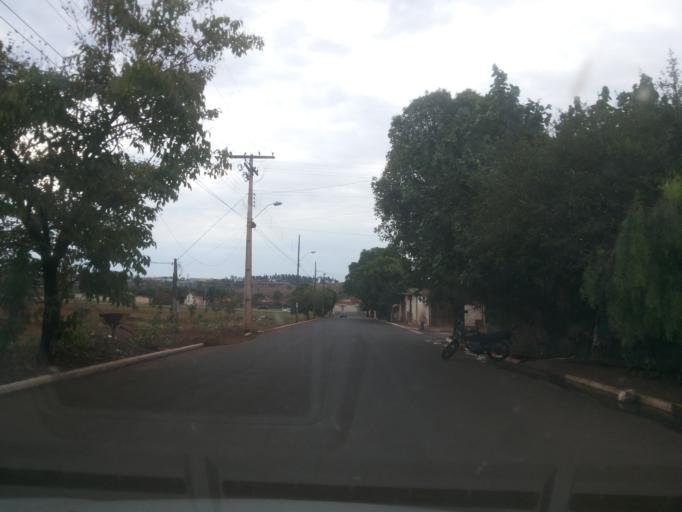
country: BR
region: Minas Gerais
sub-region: Ituiutaba
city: Ituiutaba
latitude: -18.9728
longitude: -49.4777
